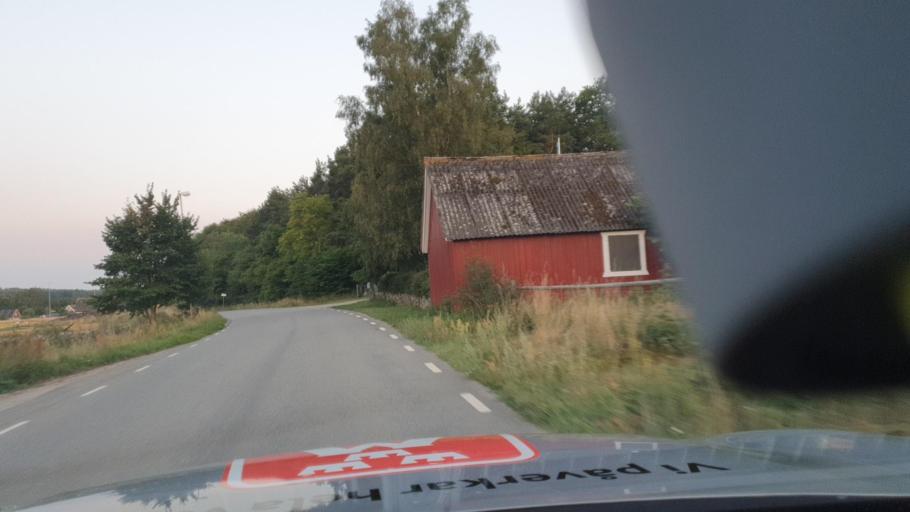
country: SE
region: Blekinge
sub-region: Solvesborgs Kommun
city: Soelvesborg
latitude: 56.0275
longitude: 14.6359
